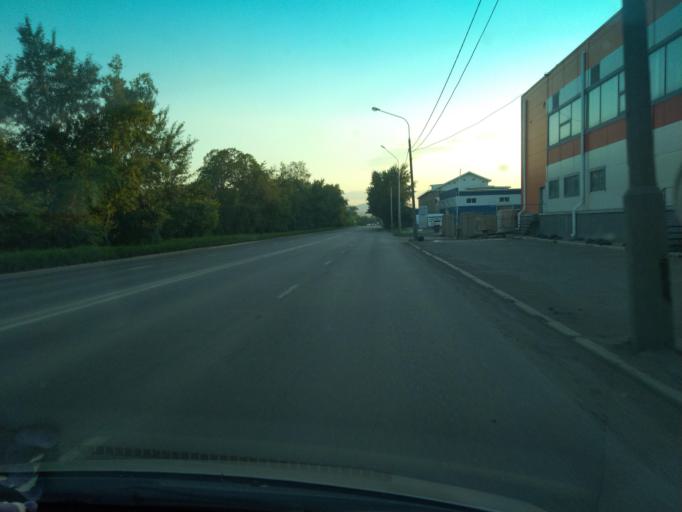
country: RU
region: Krasnoyarskiy
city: Krasnoyarsk
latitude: 55.9911
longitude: 92.9171
